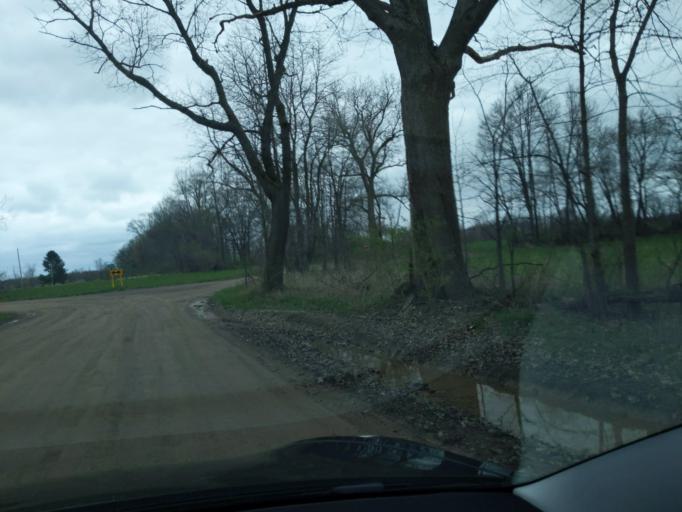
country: US
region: Michigan
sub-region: Ingham County
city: Stockbridge
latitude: 42.4463
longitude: -84.1400
